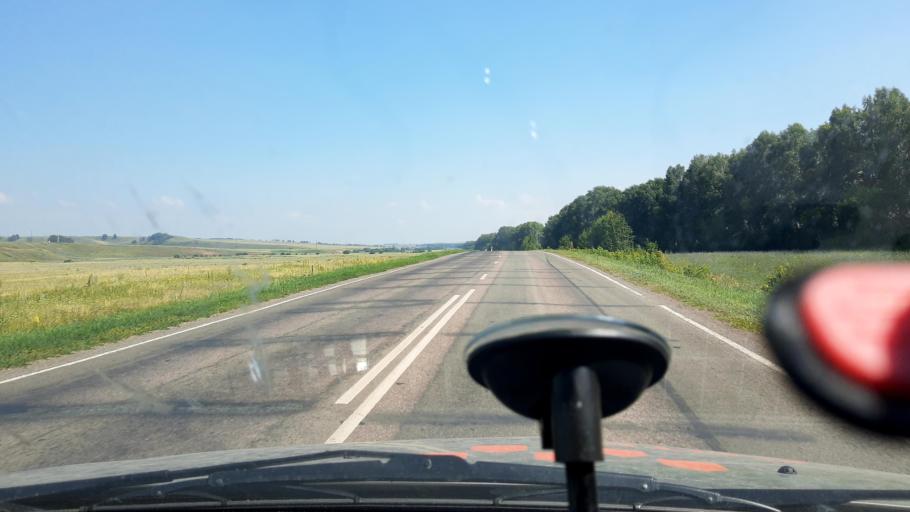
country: RU
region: Bashkortostan
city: Chekmagush
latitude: 55.1277
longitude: 54.6946
